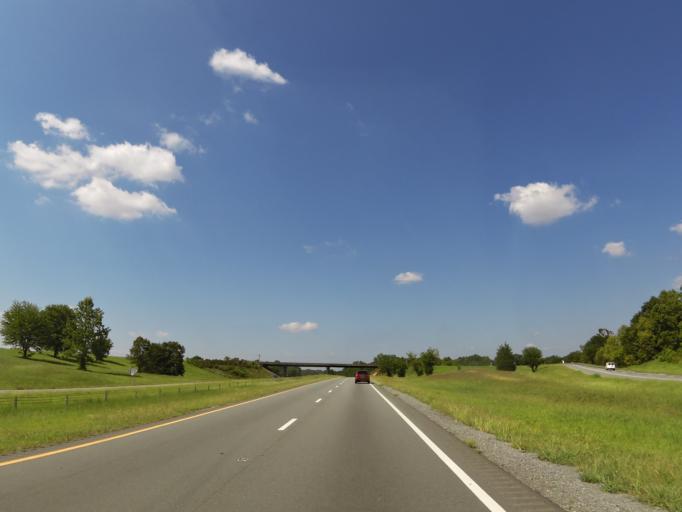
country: US
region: North Carolina
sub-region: Gaston County
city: Dallas
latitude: 35.3755
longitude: -81.2026
